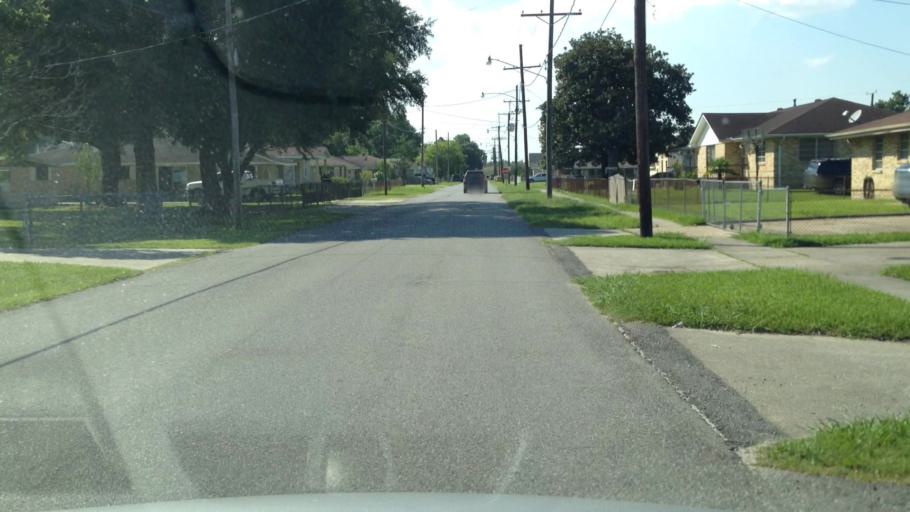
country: US
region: Louisiana
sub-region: Jefferson Parish
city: Bridge City
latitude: 29.9319
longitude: -90.1686
